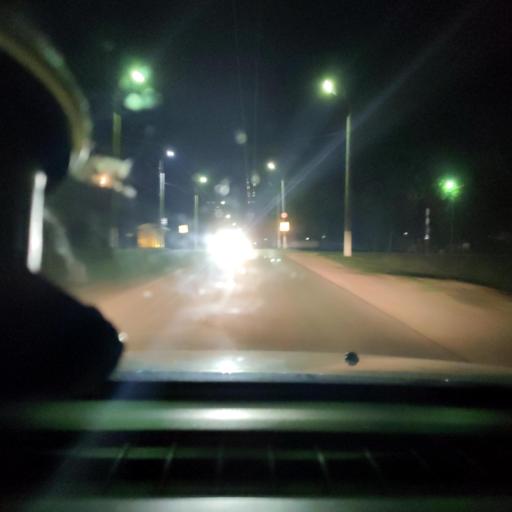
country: RU
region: Samara
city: Novokuybyshevsk
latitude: 53.0685
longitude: 49.8818
